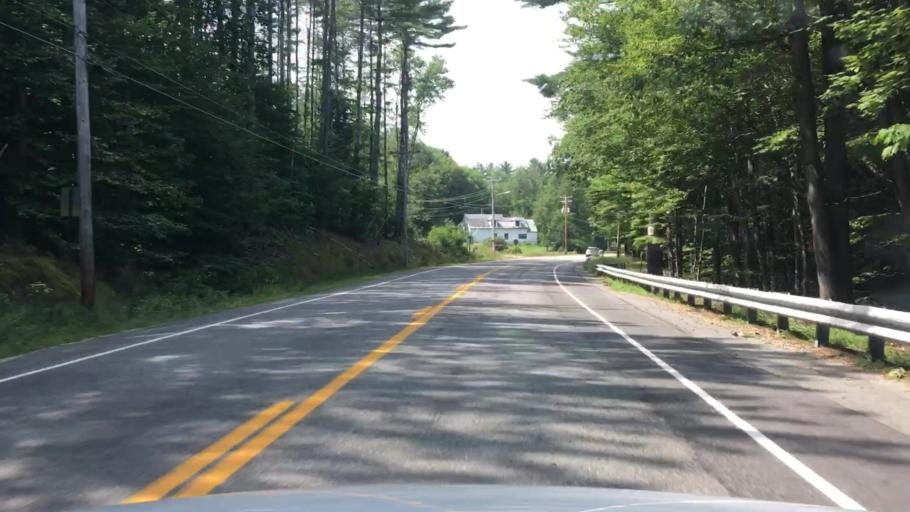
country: US
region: Maine
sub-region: Oxford County
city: Mexico
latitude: 44.5288
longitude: -70.5064
